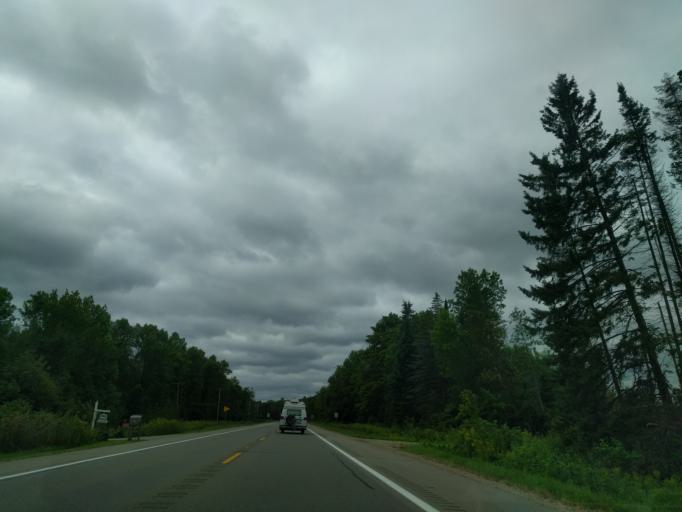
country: US
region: Michigan
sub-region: Menominee County
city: Menominee
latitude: 45.2099
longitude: -87.5301
